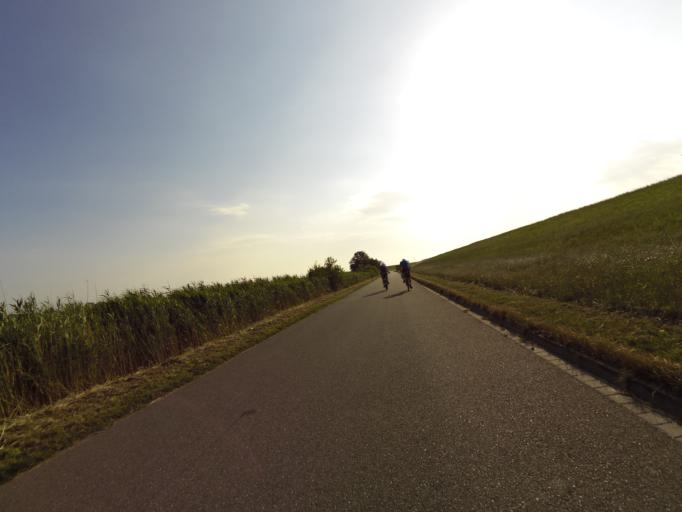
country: DE
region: Lower Saxony
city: Nordholz
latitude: 53.8095
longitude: 8.5769
